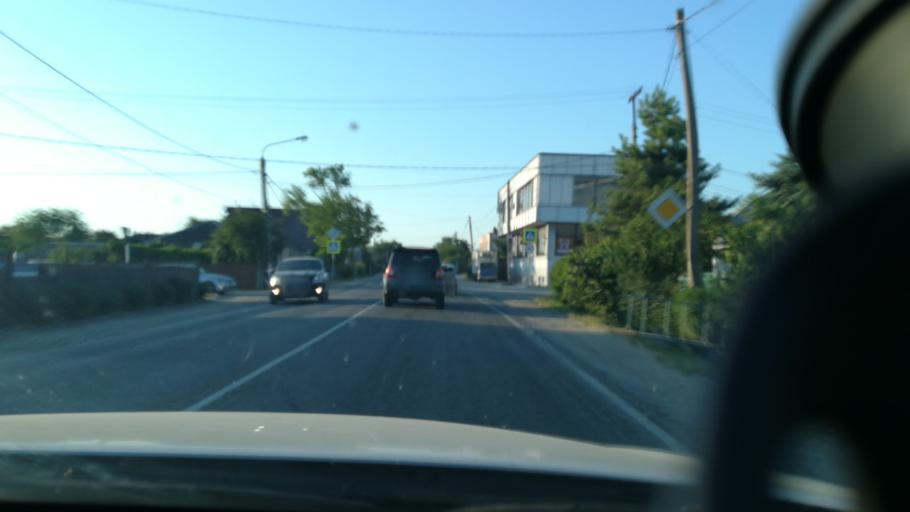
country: RU
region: Krasnodarskiy
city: Gostagayevskaya
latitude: 45.0209
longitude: 37.5028
